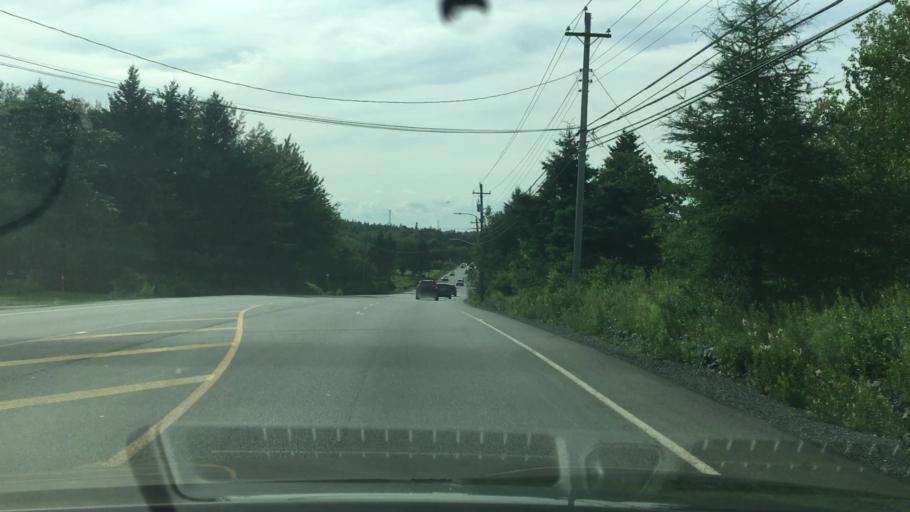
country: CA
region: Nova Scotia
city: Dartmouth
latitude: 44.7265
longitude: -63.7425
